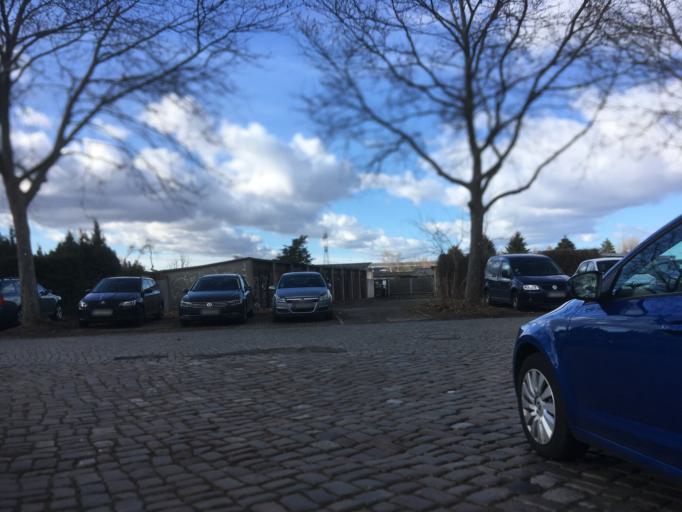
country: DE
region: Berlin
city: Oberschoneweide
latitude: 52.4698
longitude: 13.5090
